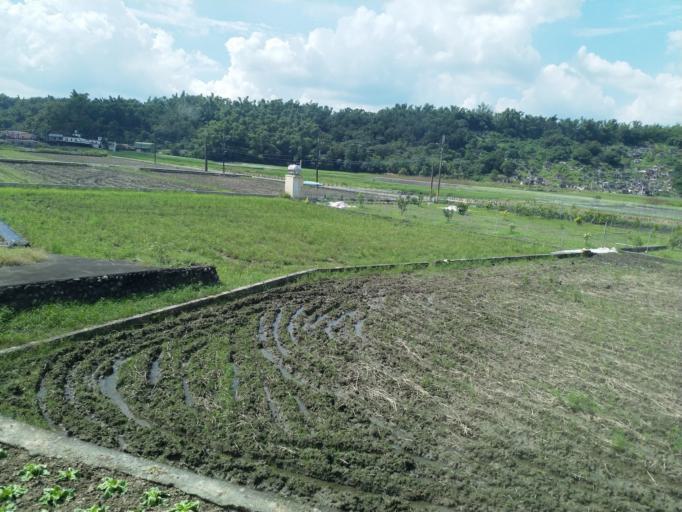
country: TW
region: Taiwan
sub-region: Pingtung
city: Pingtung
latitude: 22.8963
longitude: 120.5795
